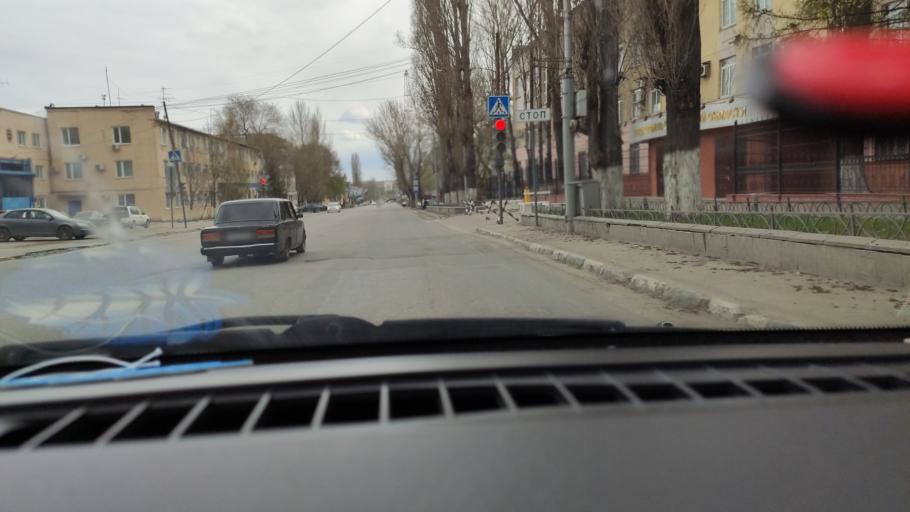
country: RU
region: Saratov
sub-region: Saratovskiy Rayon
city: Saratov
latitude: 51.5523
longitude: 46.0095
